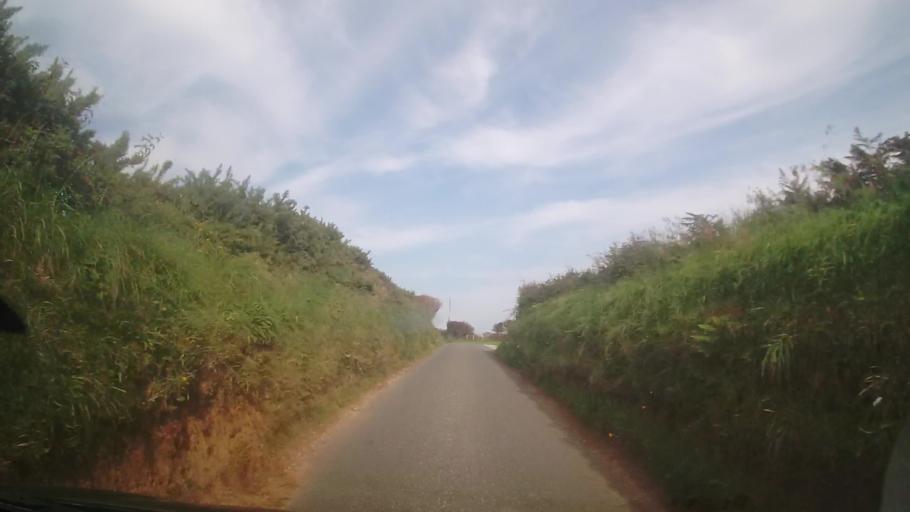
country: GB
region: Wales
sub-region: Pembrokeshire
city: Camrose
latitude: 51.8524
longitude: -5.0638
